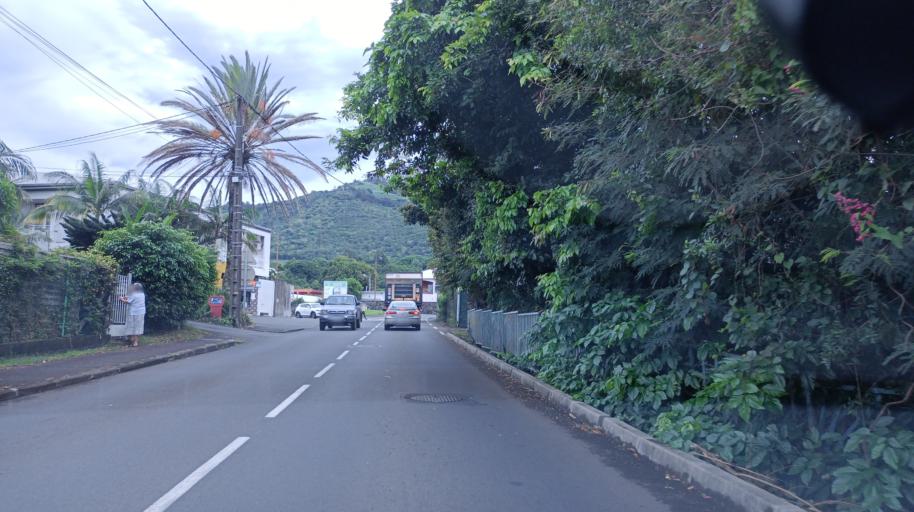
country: RE
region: Reunion
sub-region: Reunion
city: Saint-Joseph
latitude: -21.3744
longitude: 55.6152
